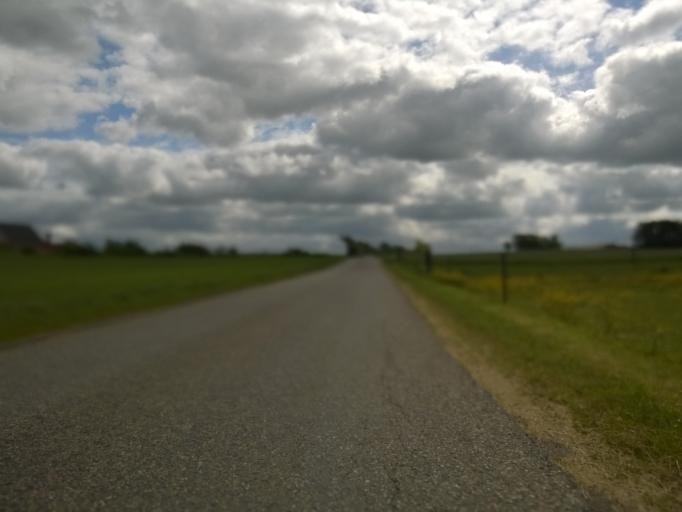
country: DK
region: Central Jutland
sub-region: Holstebro Kommune
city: Vinderup
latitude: 56.4140
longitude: 8.8203
